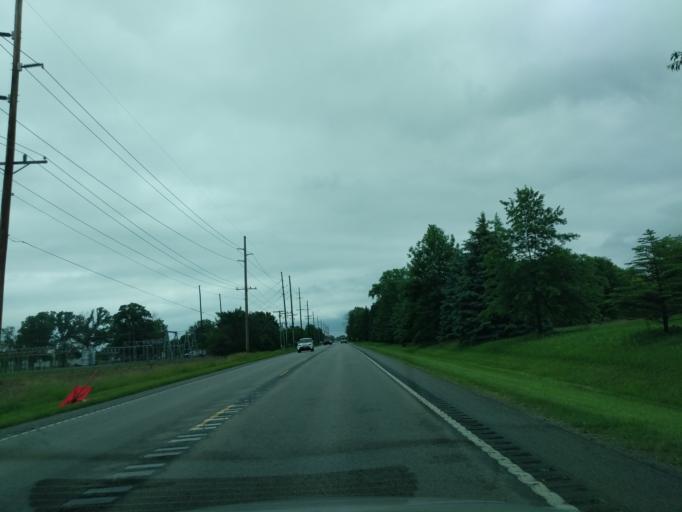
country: US
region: Indiana
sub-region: Hamilton County
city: Cicero
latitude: 40.1002
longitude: -86.0139
